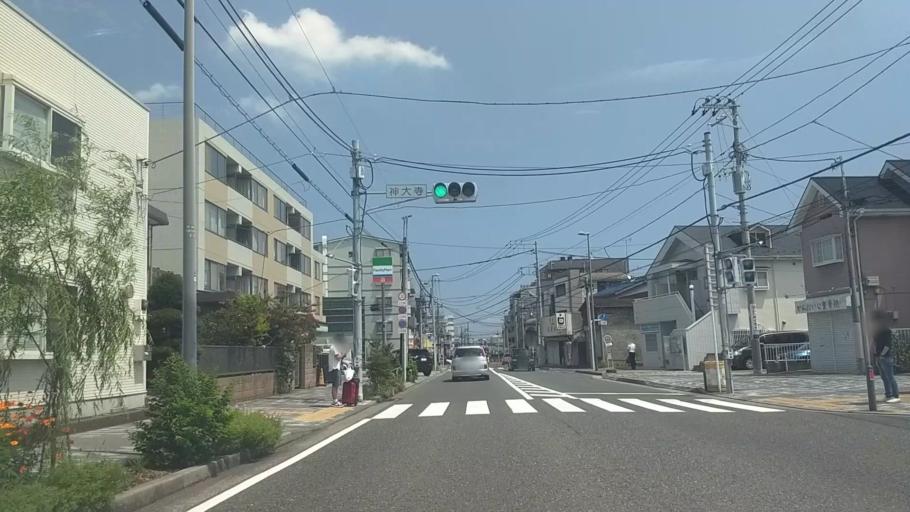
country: JP
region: Kanagawa
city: Yokohama
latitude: 35.4870
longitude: 139.6147
